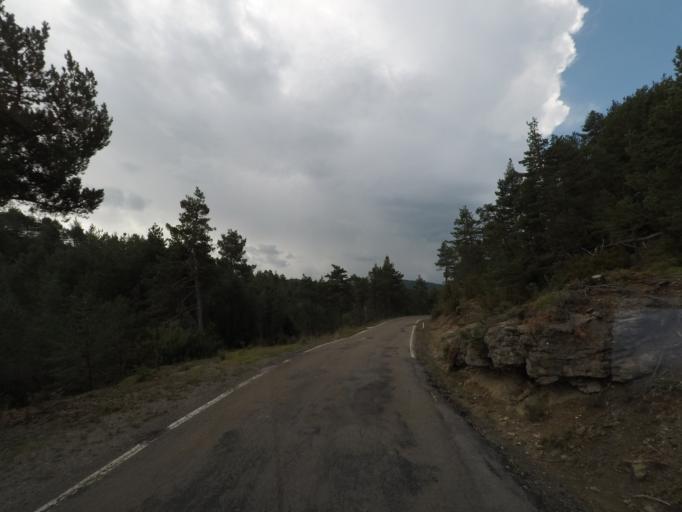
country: ES
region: Aragon
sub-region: Provincia de Huesca
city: Fiscal
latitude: 42.4044
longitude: -0.0708
